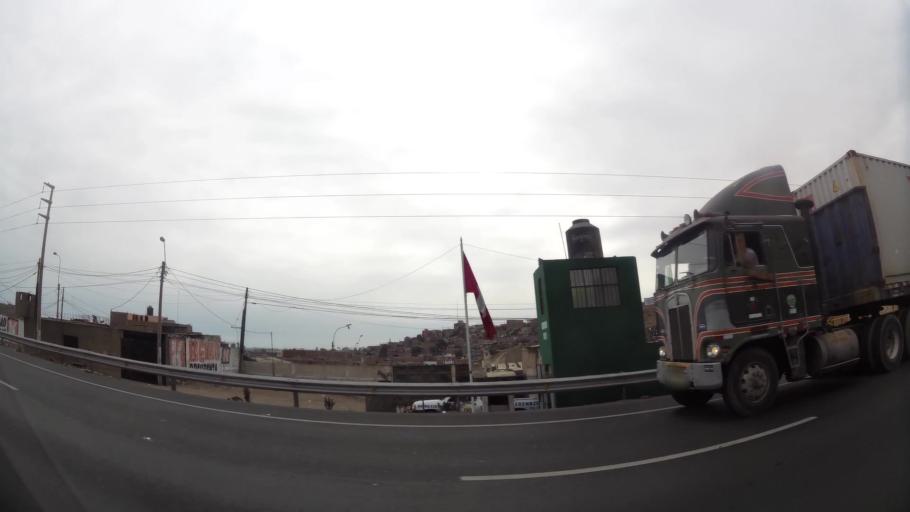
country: PE
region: Lima
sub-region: Lima
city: Surco
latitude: -12.2062
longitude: -76.9750
